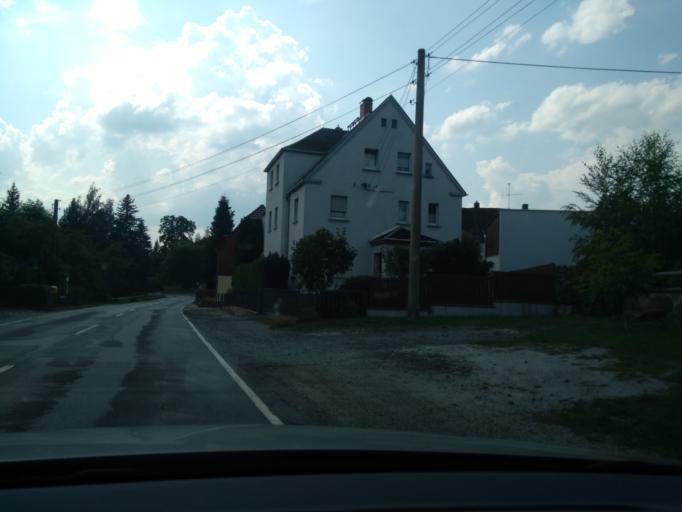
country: DE
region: Saxony
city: Oppach
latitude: 51.0636
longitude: 14.5104
